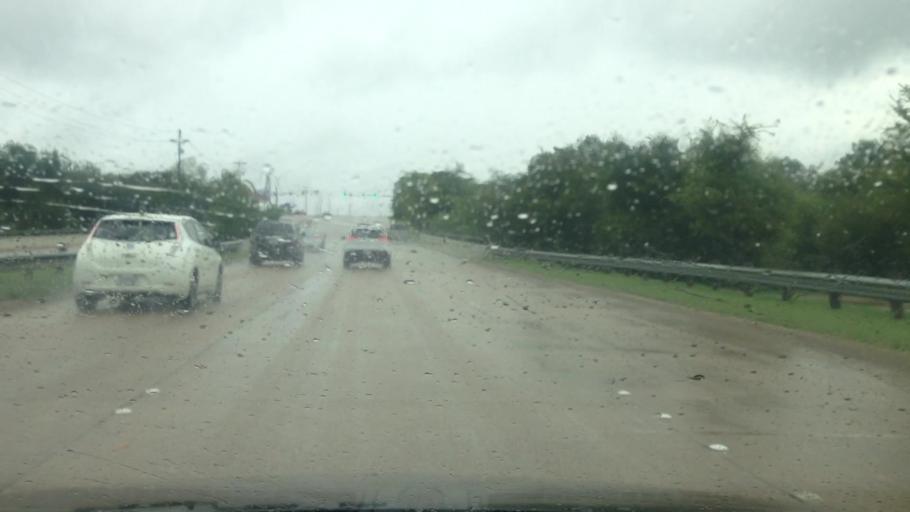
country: US
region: Texas
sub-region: Tarrant County
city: Watauga
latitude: 32.8606
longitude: -97.2699
